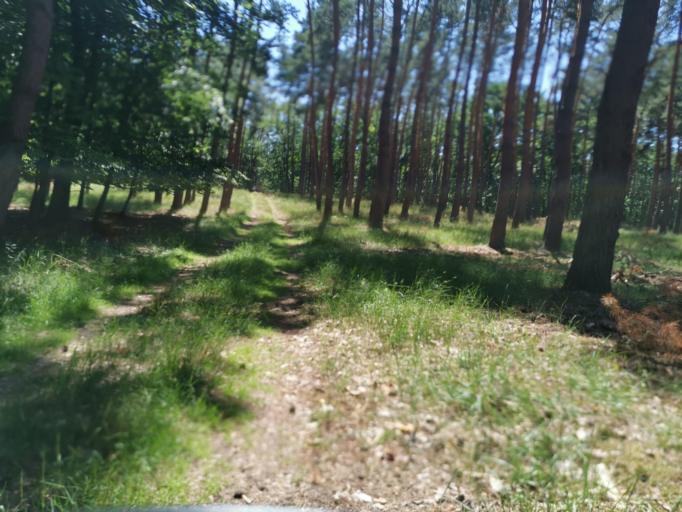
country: CZ
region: South Moravian
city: Bzenec
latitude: 48.9321
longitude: 17.2533
